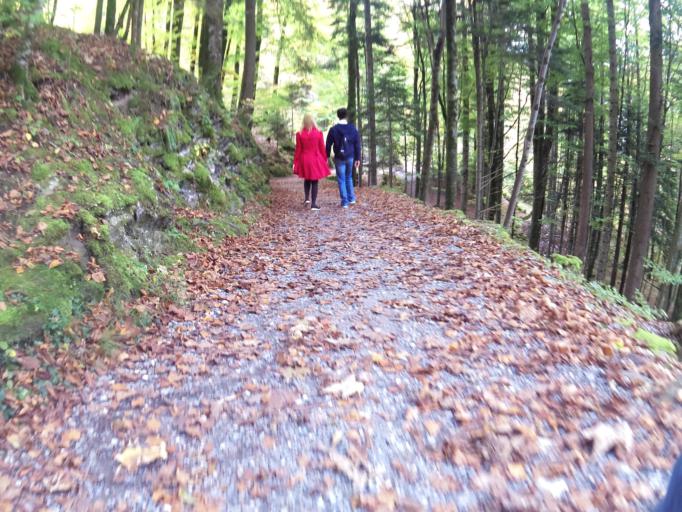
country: CH
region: Bern
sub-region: Interlaken-Oberhasli District
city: Brienz
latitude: 46.7353
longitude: 8.0222
